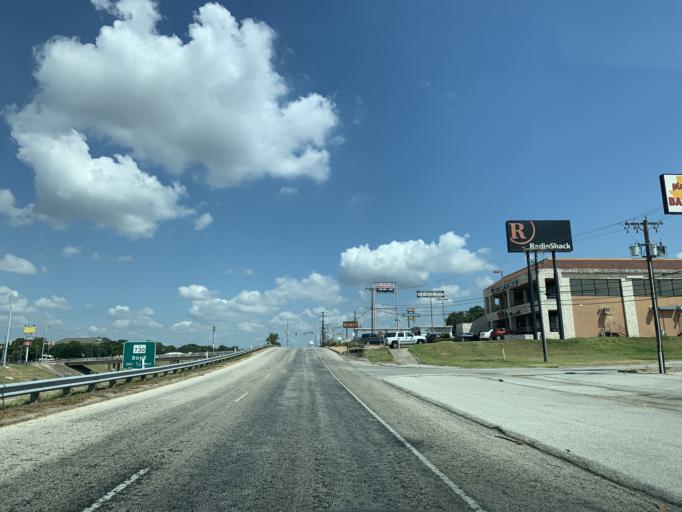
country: US
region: Texas
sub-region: Tarrant County
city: Azle
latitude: 32.8906
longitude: -97.5396
